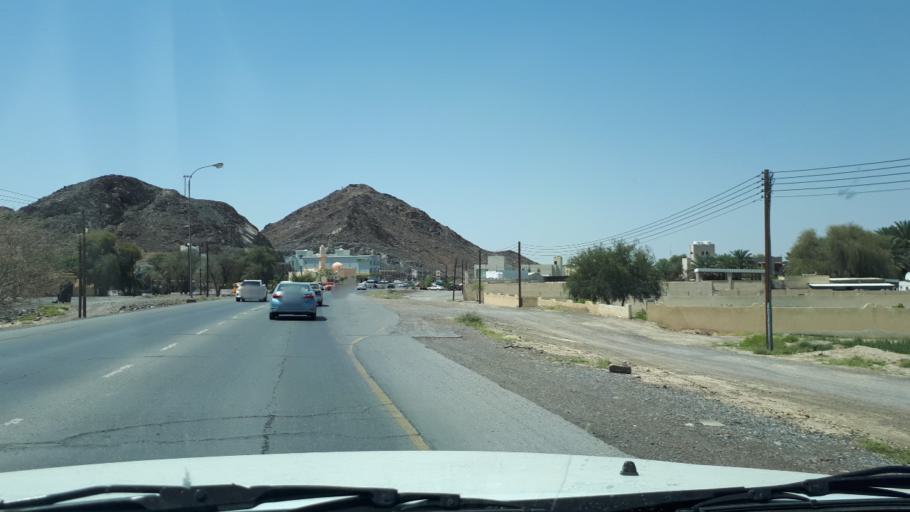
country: OM
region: Muhafazat ad Dakhiliyah
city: Bahla'
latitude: 22.9819
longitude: 57.3086
